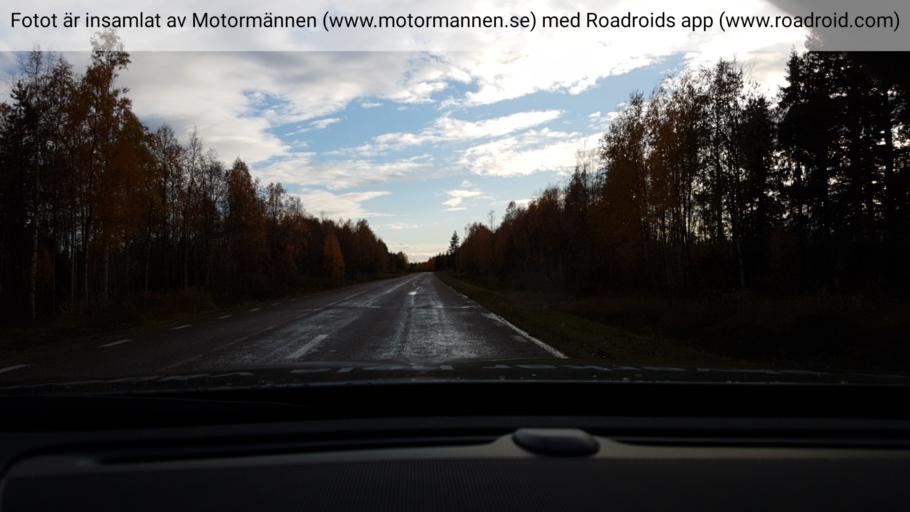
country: SE
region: Norrbotten
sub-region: Pajala Kommun
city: Pajala
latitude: 67.1458
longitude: 22.6219
